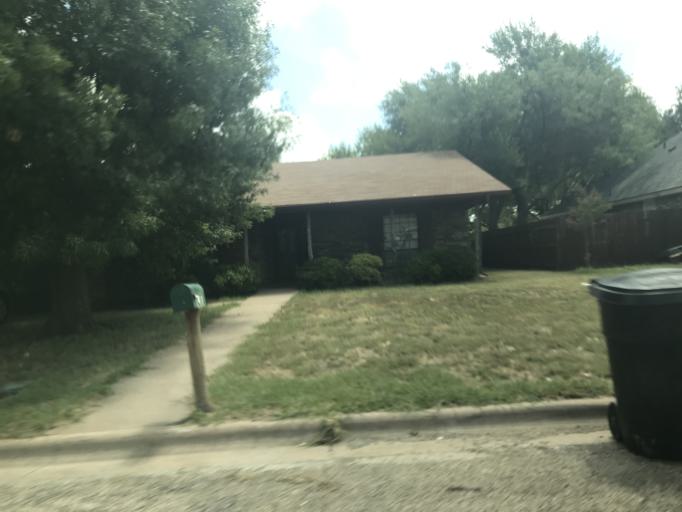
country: US
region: Texas
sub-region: Taylor County
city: Abilene
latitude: 32.4401
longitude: -99.6978
